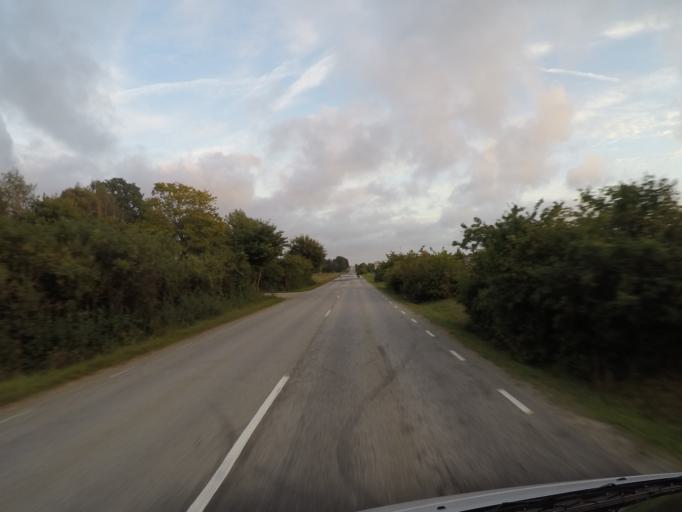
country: SE
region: Skane
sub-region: Lunds Kommun
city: Lund
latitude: 55.7136
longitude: 13.2469
